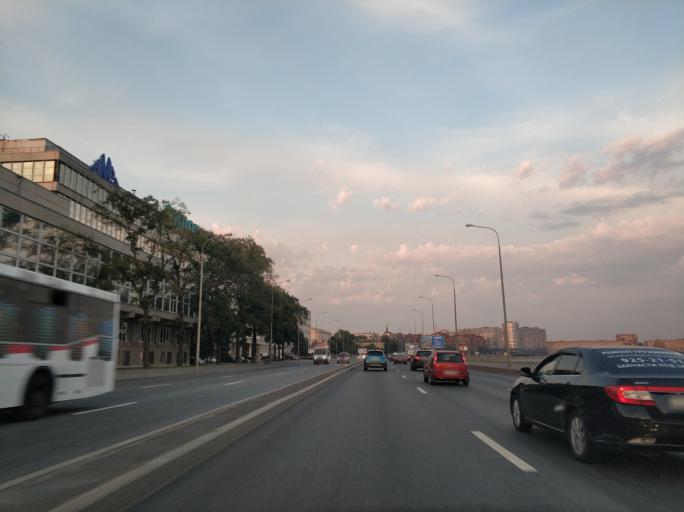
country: RU
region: Leningrad
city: Finlyandskiy
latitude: 59.9598
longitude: 30.3888
